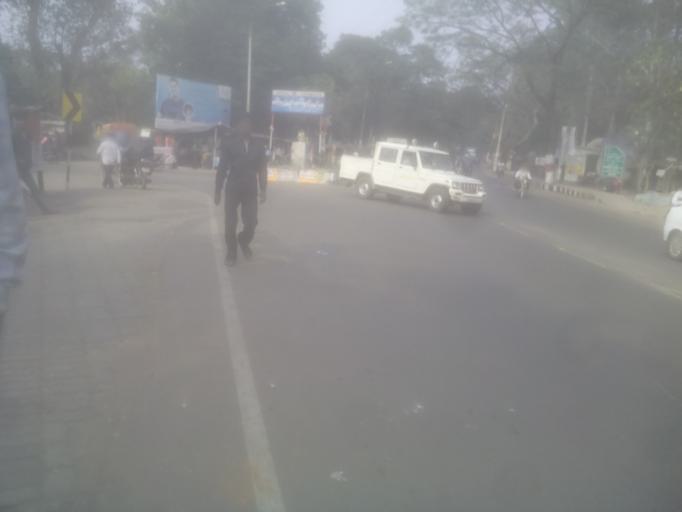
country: IN
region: Jharkhand
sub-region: Dhanbad
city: Dhanbad
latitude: 23.8014
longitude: 86.4268
